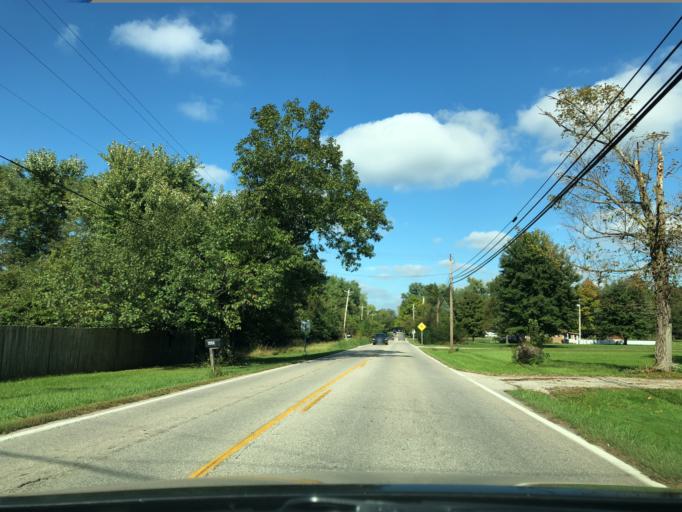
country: US
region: Ohio
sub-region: Hamilton County
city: Loveland
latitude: 39.2491
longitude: -84.2528
